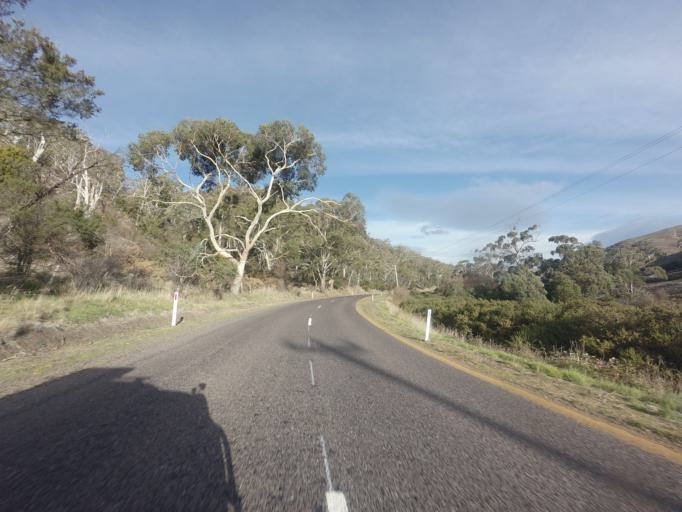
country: AU
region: Tasmania
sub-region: Brighton
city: Bridgewater
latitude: -42.4456
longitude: 147.1539
